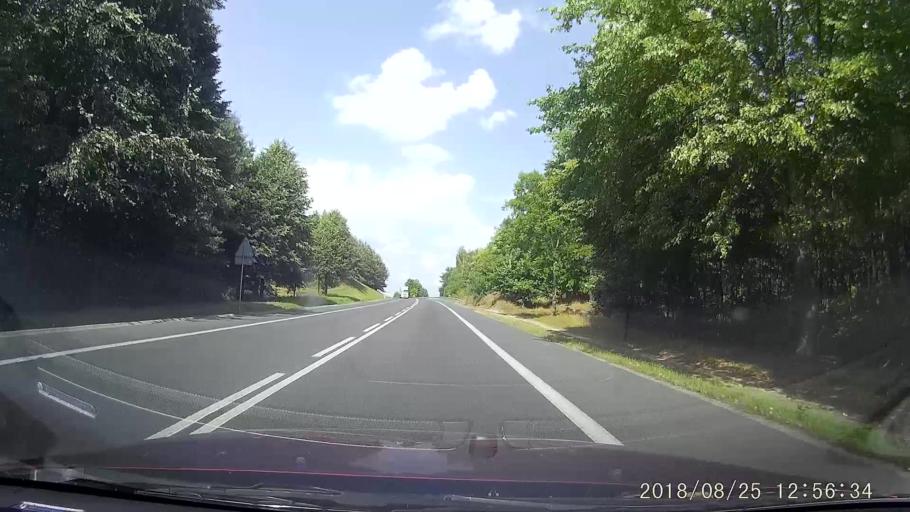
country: PL
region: West Pomeranian Voivodeship
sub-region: Powiat goleniowski
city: Przybiernow
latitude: 53.7420
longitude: 14.7757
